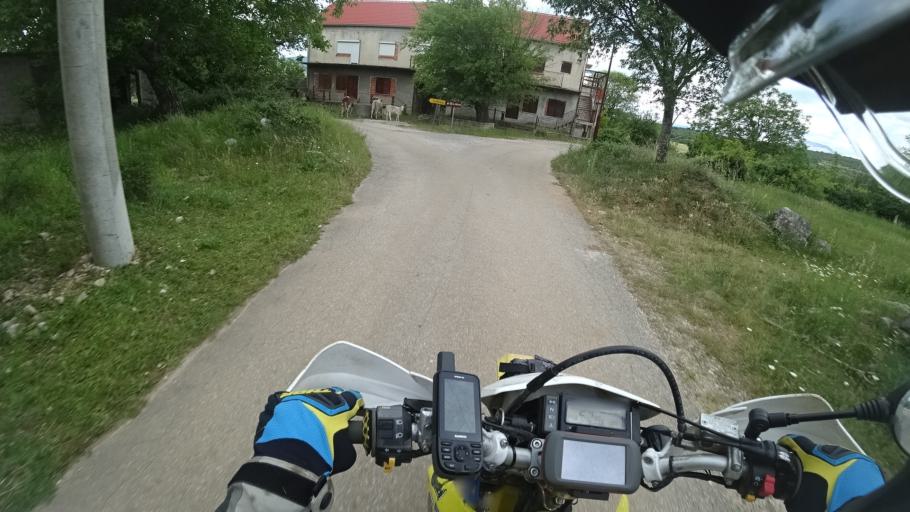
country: HR
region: Sibensko-Kniniska
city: Kistanje
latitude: 44.1084
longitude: 15.9397
